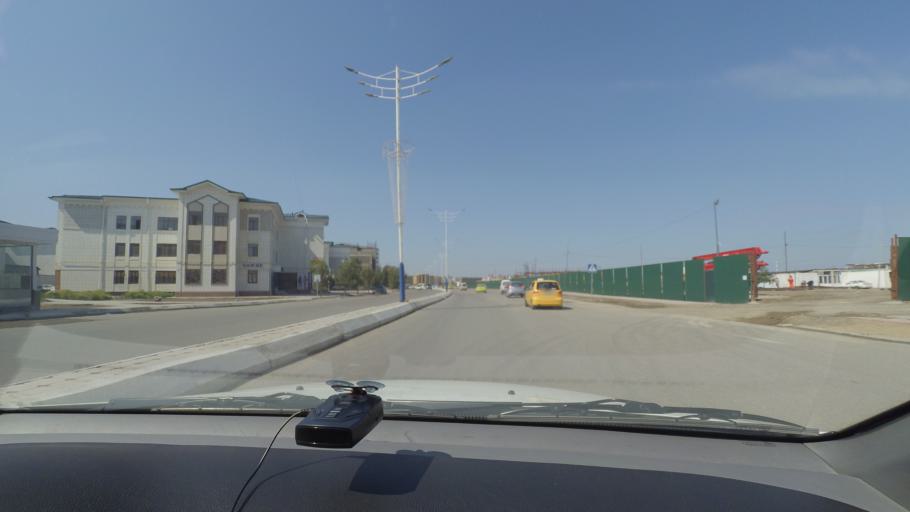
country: UZ
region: Bukhara
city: Bukhara
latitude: 39.7808
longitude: 64.4328
